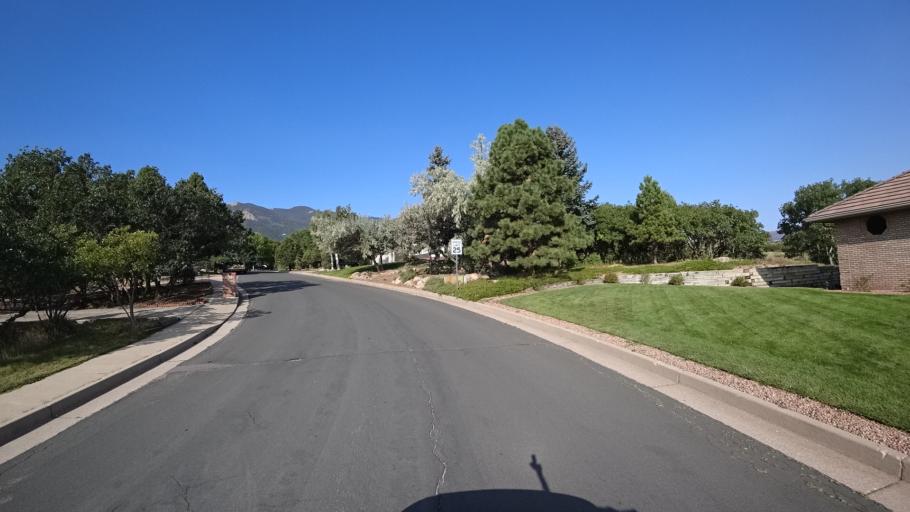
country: US
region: Colorado
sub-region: El Paso County
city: Colorado Springs
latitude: 38.8242
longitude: -104.8739
